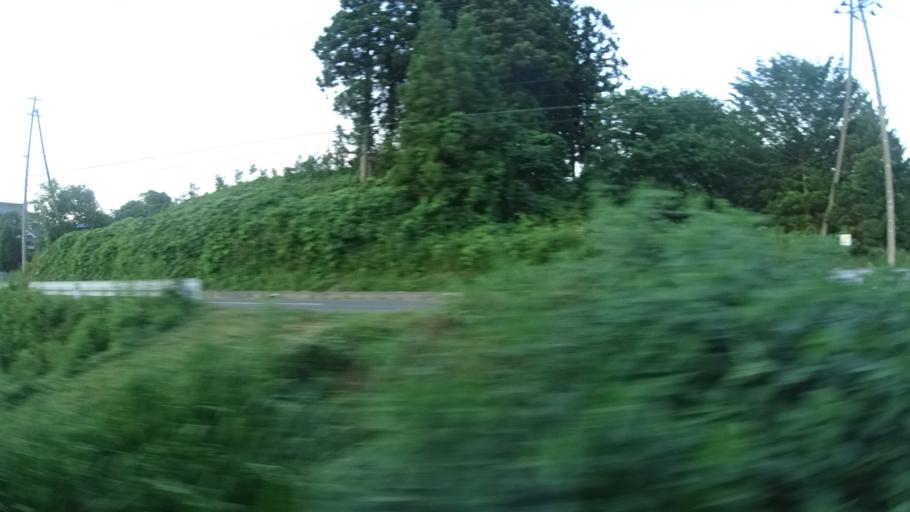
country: JP
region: Fukushima
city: Funehikimachi-funehiki
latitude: 37.4008
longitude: 140.6205
